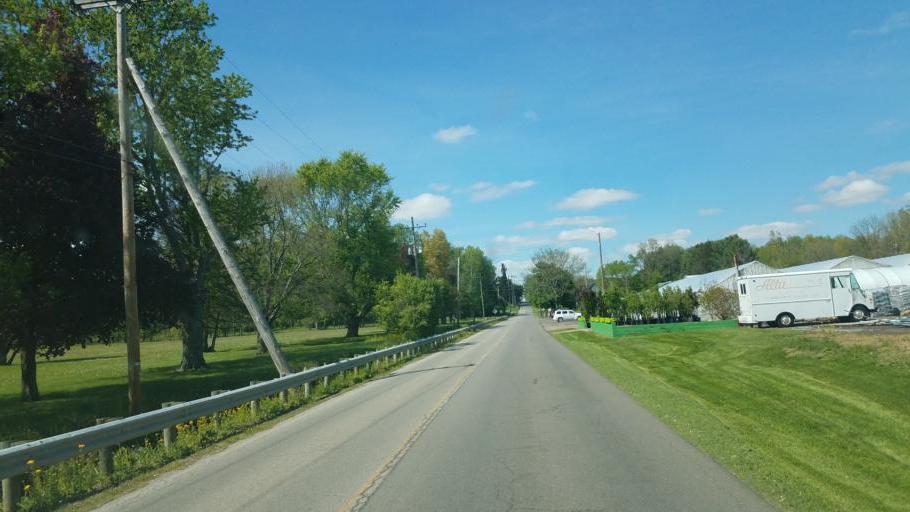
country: US
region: Ohio
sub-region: Richland County
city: Ontario
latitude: 40.7325
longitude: -82.5707
